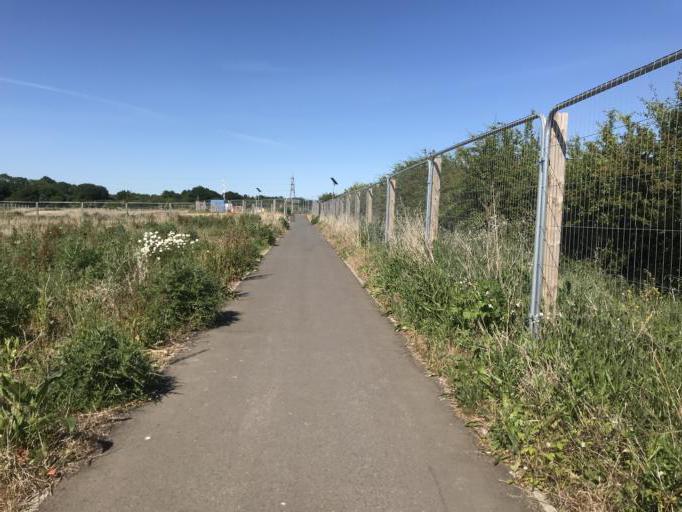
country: GB
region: England
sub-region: Cambridgeshire
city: Histon
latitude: 52.2299
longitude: 0.1066
